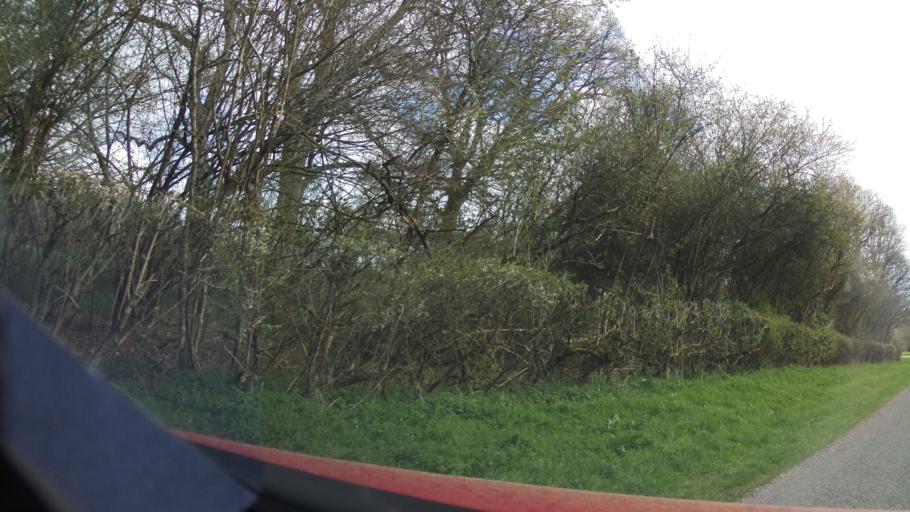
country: GB
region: England
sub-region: Hampshire
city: Highclere
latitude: 51.3089
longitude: -1.4597
